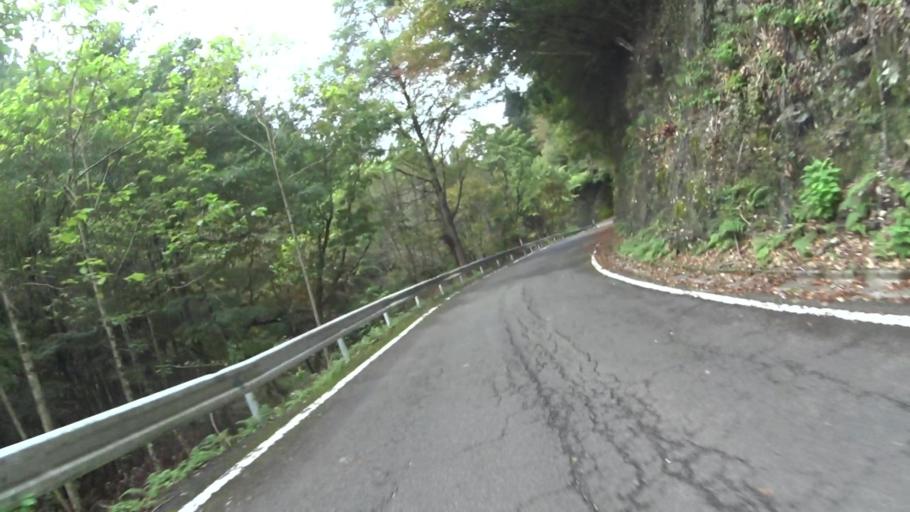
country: JP
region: Fukui
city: Obama
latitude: 35.2744
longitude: 135.7152
